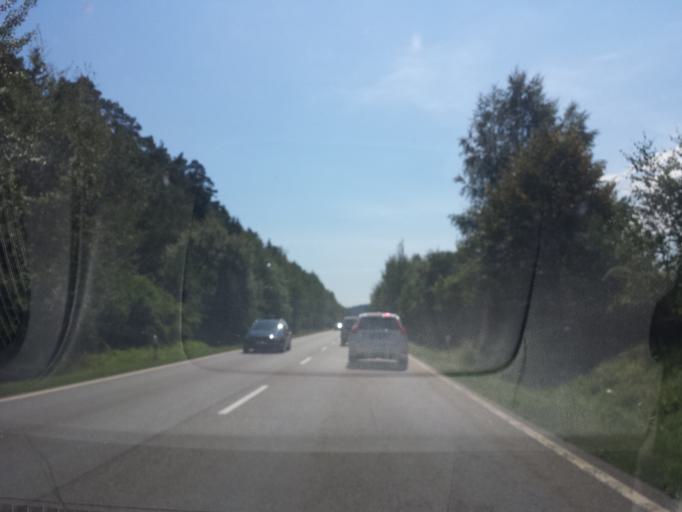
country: DE
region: Bavaria
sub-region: Lower Bavaria
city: Loitzendorf
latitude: 49.0822
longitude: 12.6401
